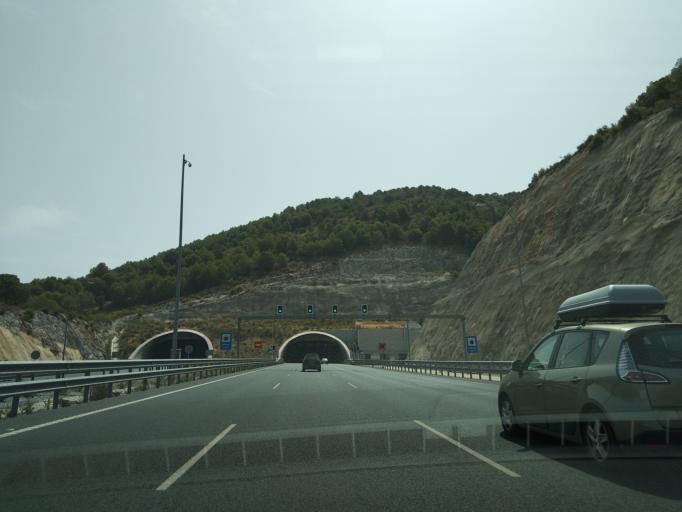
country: ES
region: Andalusia
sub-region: Provincia de Malaga
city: Alhaurin de la Torre
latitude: 36.6585
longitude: -4.5224
